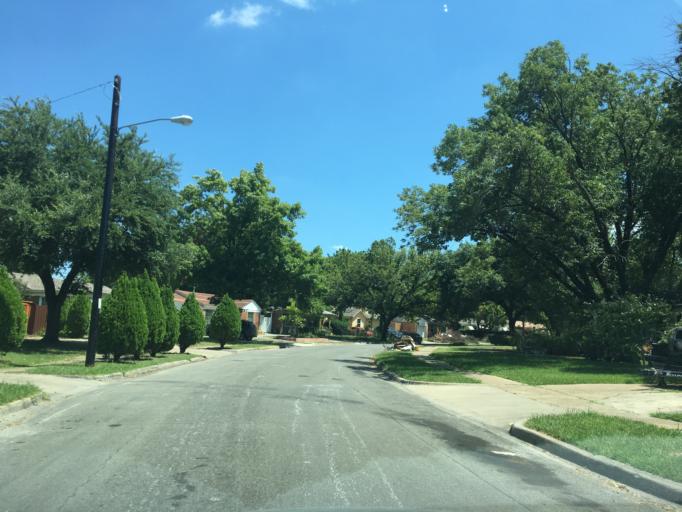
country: US
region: Texas
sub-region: Dallas County
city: Garland
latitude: 32.8414
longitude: -96.6851
